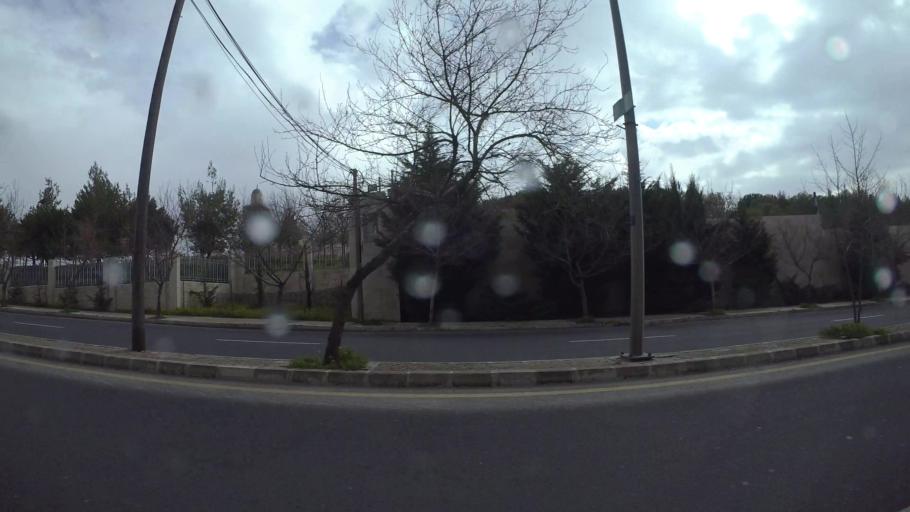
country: JO
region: Amman
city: Wadi as Sir
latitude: 31.9845
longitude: 35.8207
